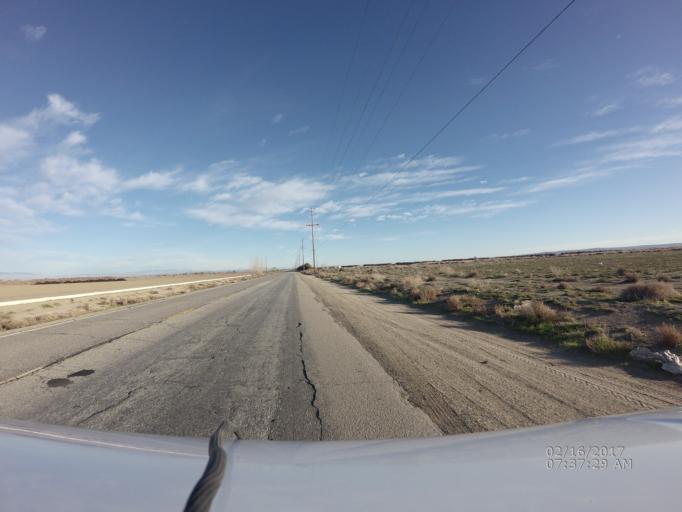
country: US
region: California
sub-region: Los Angeles County
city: Littlerock
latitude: 34.6666
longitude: -117.9697
